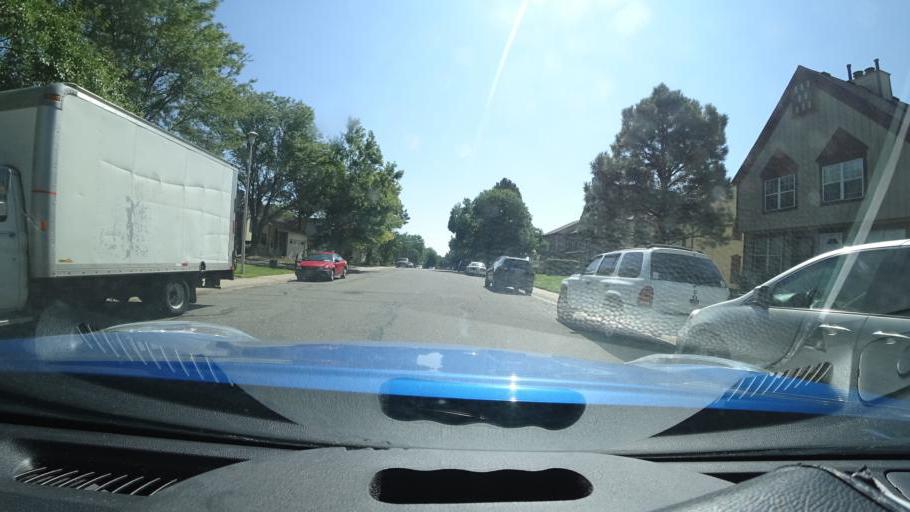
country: US
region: Colorado
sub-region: Adams County
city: Aurora
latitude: 39.6870
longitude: -104.8218
